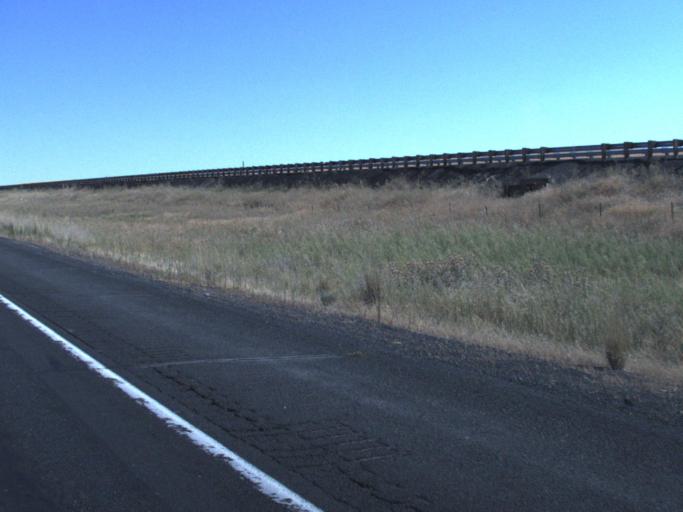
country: US
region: Washington
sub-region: Adams County
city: Ritzville
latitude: 47.1103
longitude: -118.5482
